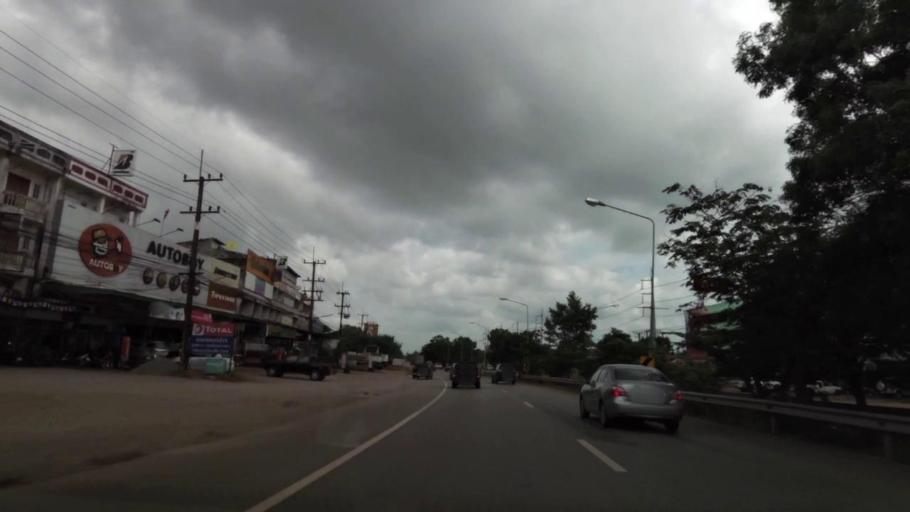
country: TH
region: Chanthaburi
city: Na Yai Am
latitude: 12.7804
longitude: 101.8196
